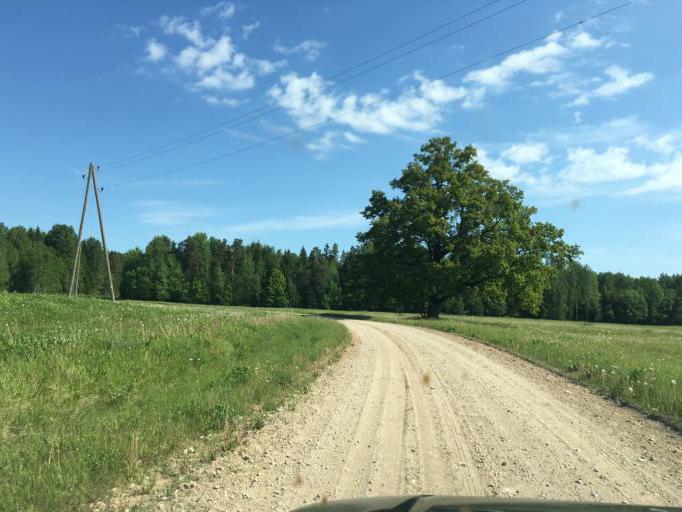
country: LV
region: Talsu Rajons
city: Talsi
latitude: 57.3165
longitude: 22.4441
